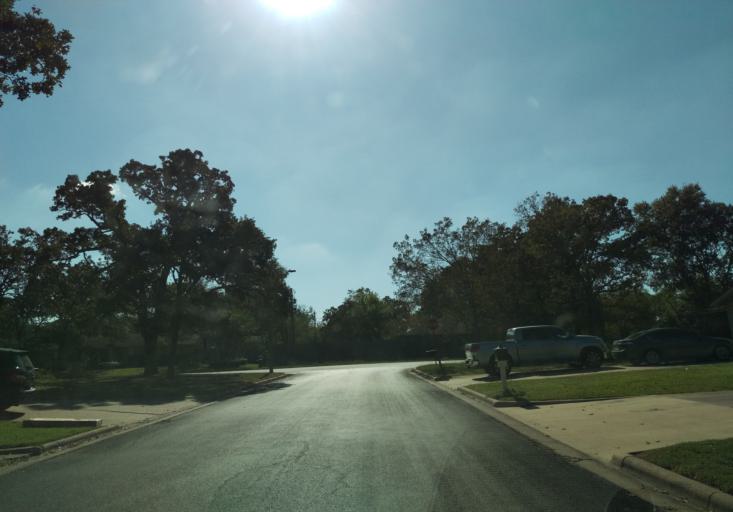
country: US
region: Texas
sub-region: Brazos County
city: College Station
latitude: 30.6199
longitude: -96.2867
